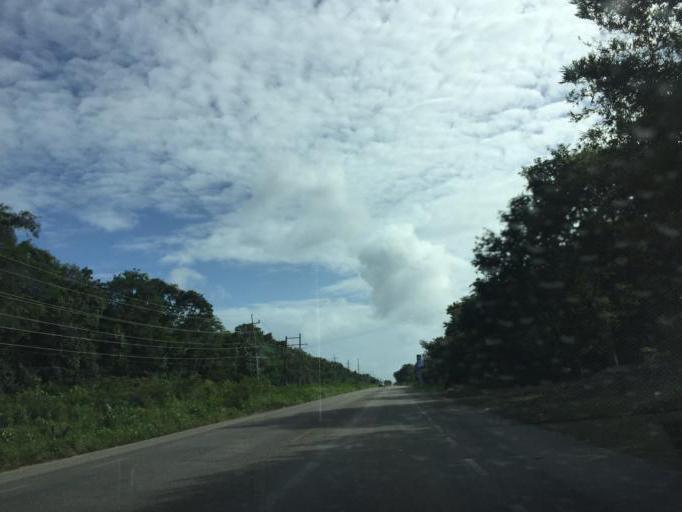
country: MX
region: Quintana Roo
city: Tulum
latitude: 20.2519
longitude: -87.4669
